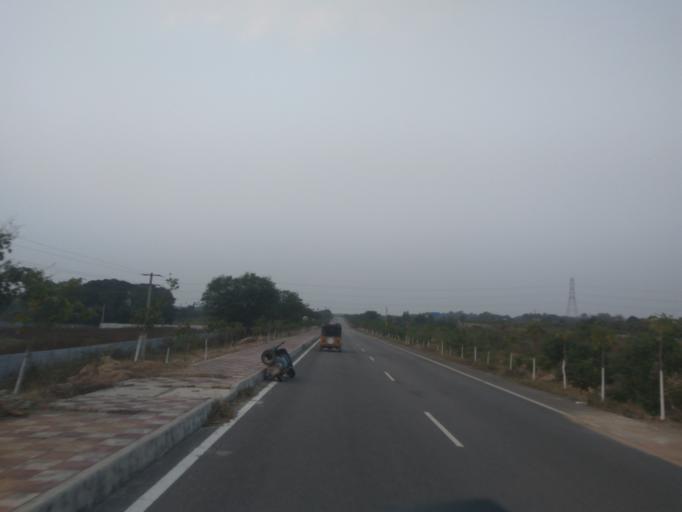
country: IN
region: Telangana
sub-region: Rangareddi
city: Secunderabad
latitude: 17.5466
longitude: 78.6297
